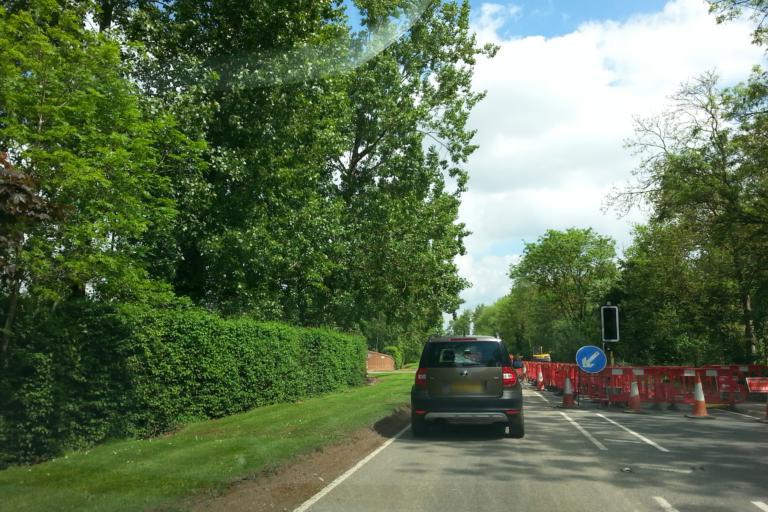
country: GB
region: England
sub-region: Cambridgeshire
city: Yaxley
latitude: 52.5317
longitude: -0.2620
